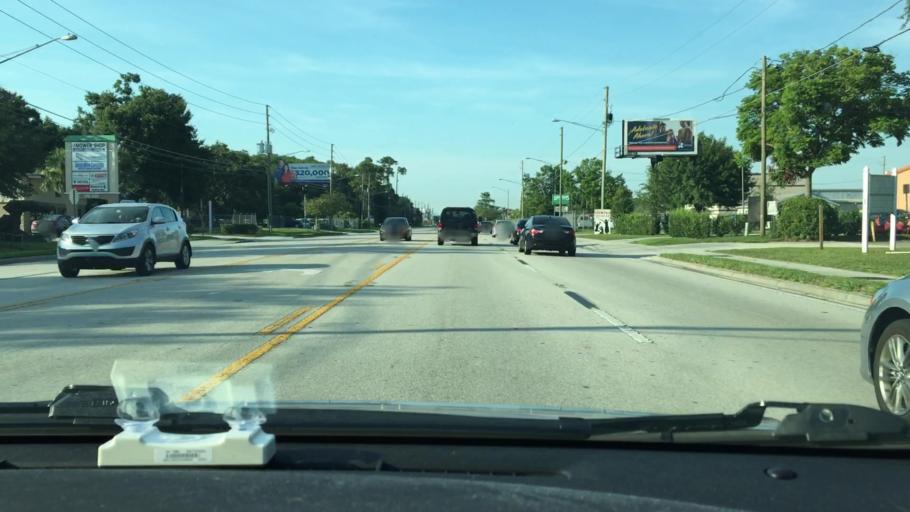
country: US
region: Florida
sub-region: Orange County
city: Azalea Park
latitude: 28.5484
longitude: -81.2859
